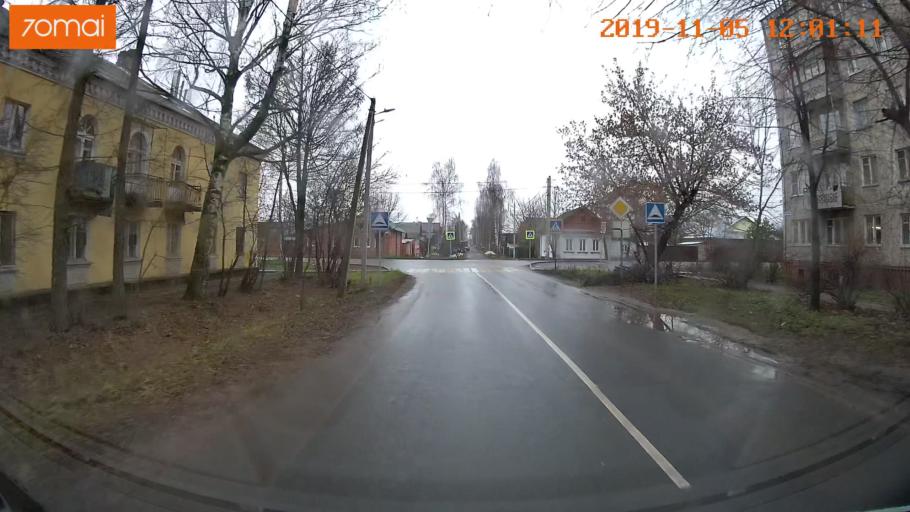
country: RU
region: Ivanovo
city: Kokhma
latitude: 56.9736
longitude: 41.0456
